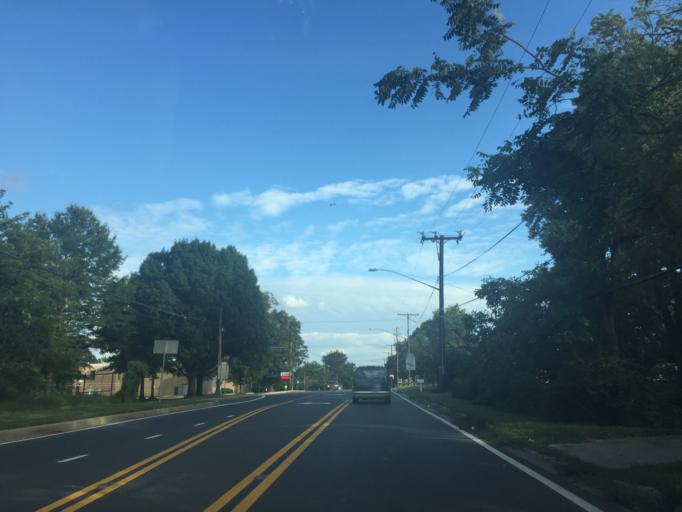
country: US
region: Maryland
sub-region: Montgomery County
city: Redland
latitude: 39.1323
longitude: -77.1212
